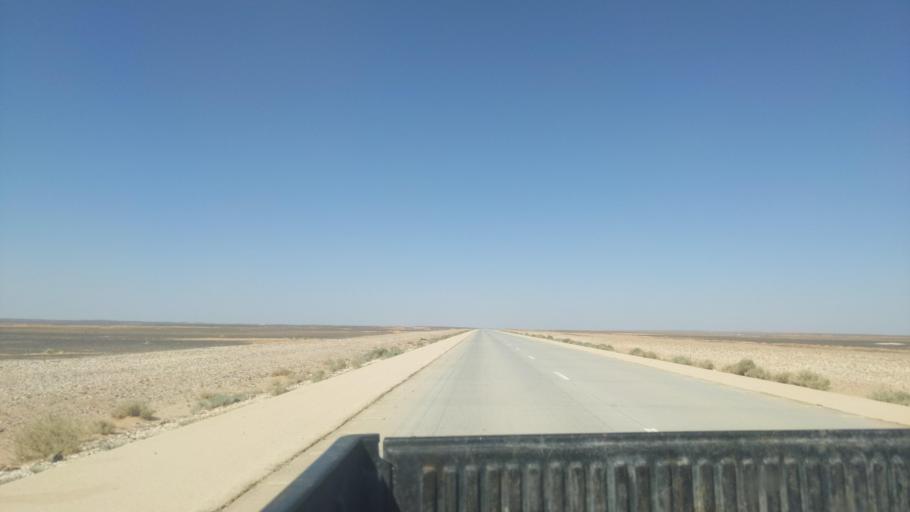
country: JO
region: Amman
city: Al Azraq ash Shamali
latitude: 31.4547
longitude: 36.7810
